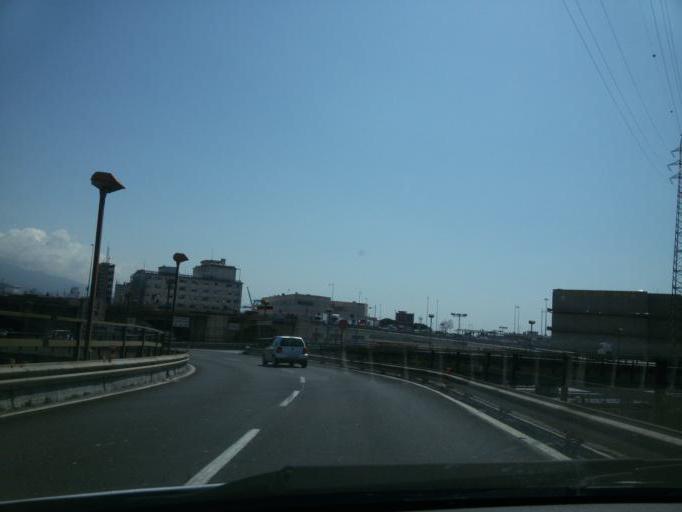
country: IT
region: Liguria
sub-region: Provincia di Genova
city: San Teodoro
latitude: 44.4096
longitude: 8.9017
